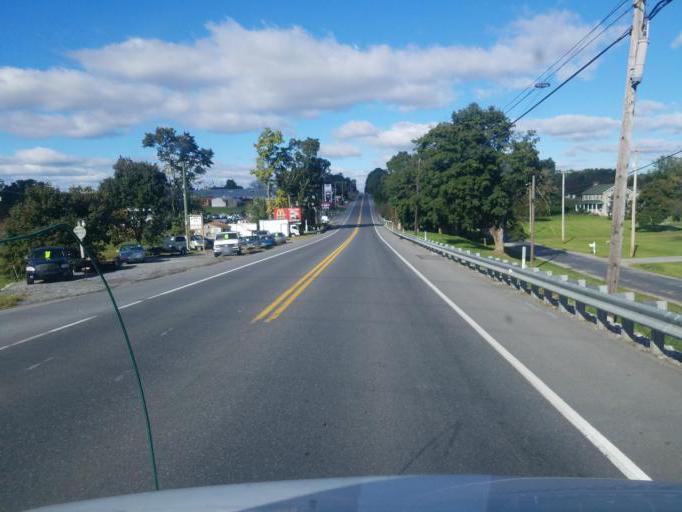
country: US
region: Pennsylvania
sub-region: Franklin County
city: Waynesboro
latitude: 39.7639
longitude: -77.6058
